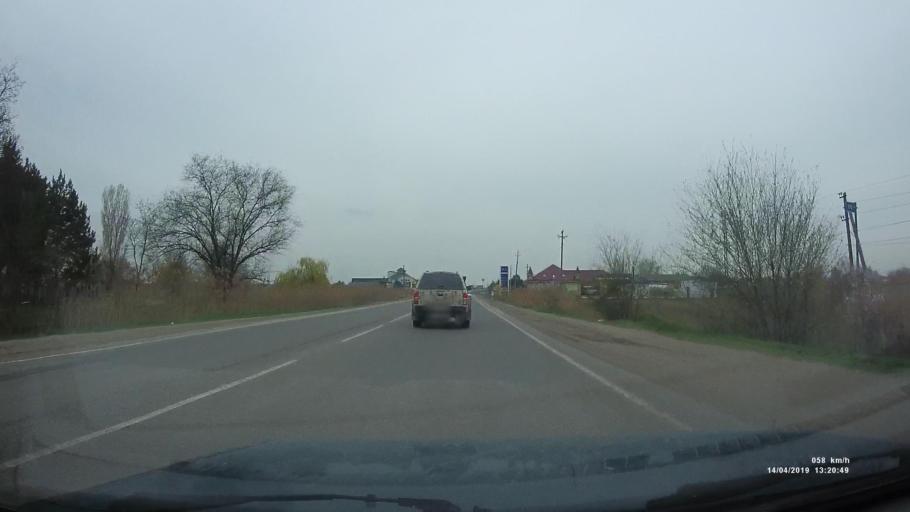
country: RU
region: Rostov
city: Kuleshovka
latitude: 47.0825
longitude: 39.5339
